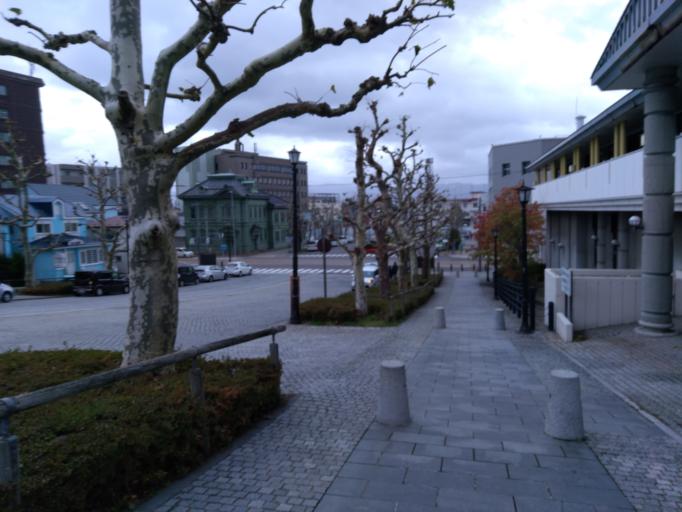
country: JP
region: Hokkaido
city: Hakodate
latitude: 41.7667
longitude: 140.7111
